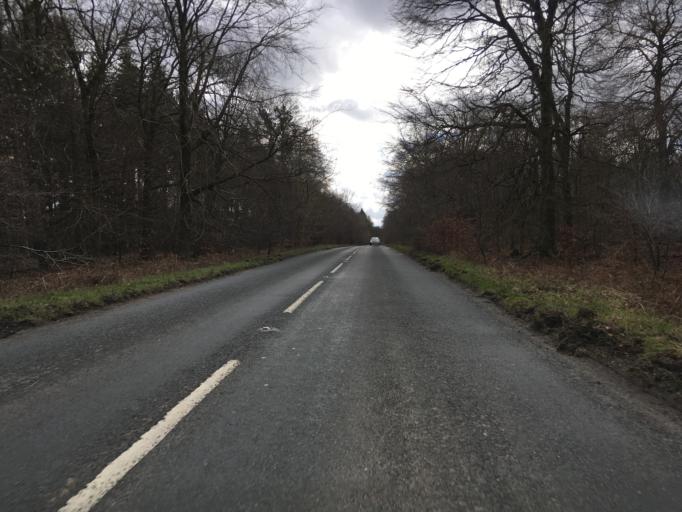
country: GB
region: England
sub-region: Gloucestershire
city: Coleford
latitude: 51.8132
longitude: -2.5933
